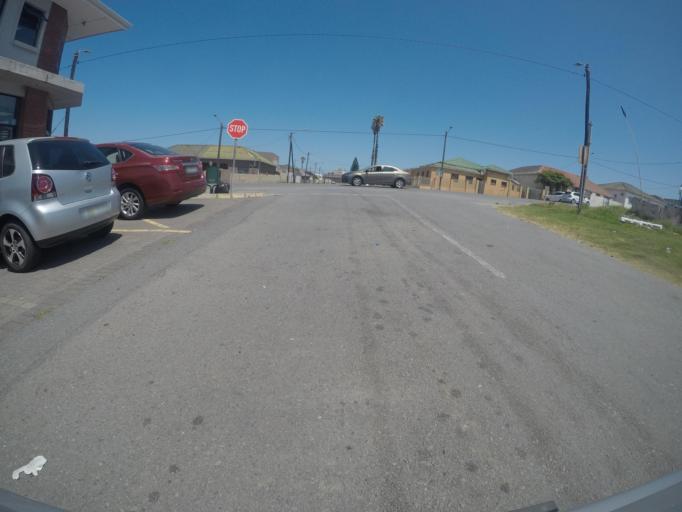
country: ZA
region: Eastern Cape
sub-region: Buffalo City Metropolitan Municipality
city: East London
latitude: -33.0121
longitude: 27.9180
